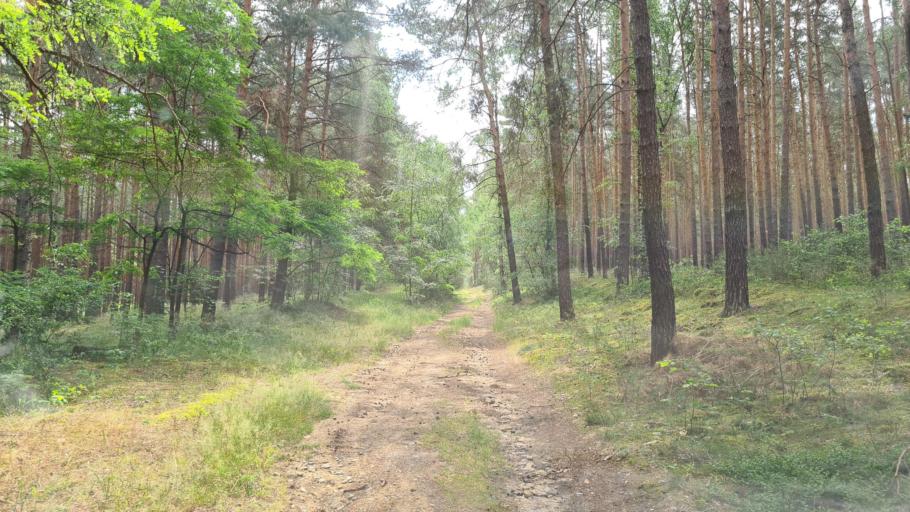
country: DE
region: Brandenburg
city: Crinitz
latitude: 51.7356
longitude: 13.7708
